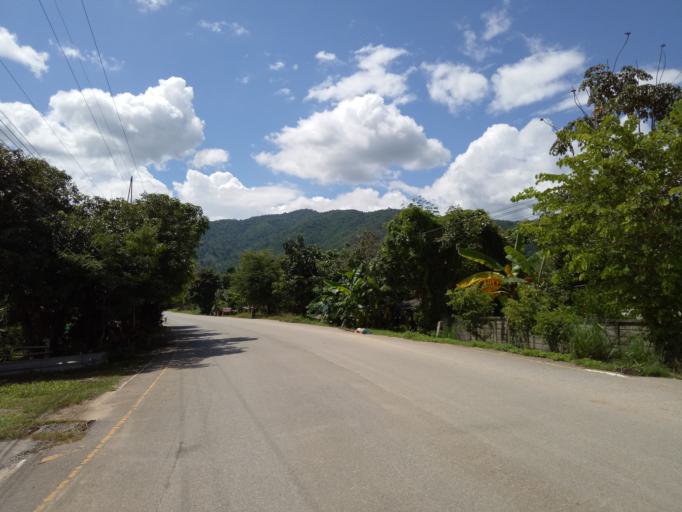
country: TH
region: Chiang Rai
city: Chiang Rai
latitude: 19.9942
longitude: 99.8268
